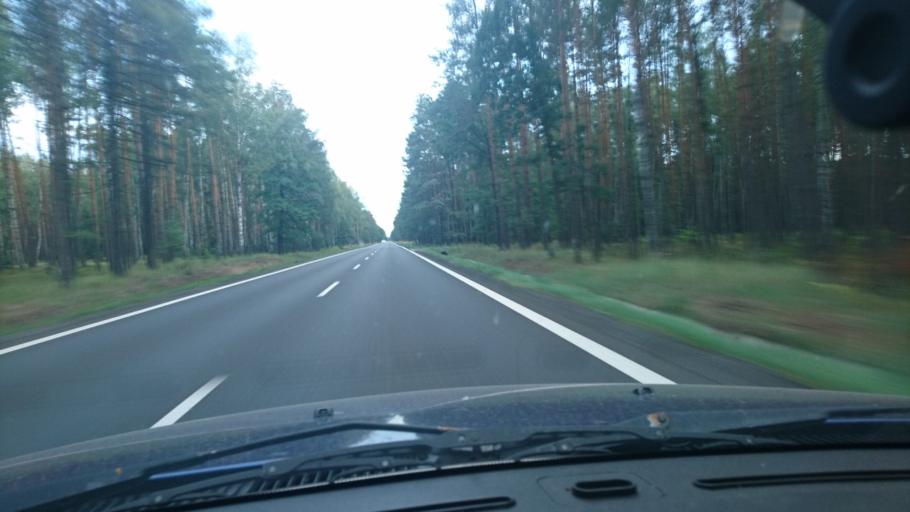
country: PL
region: Silesian Voivodeship
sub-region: Powiat tarnogorski
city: Tworog
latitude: 50.5684
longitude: 18.7114
